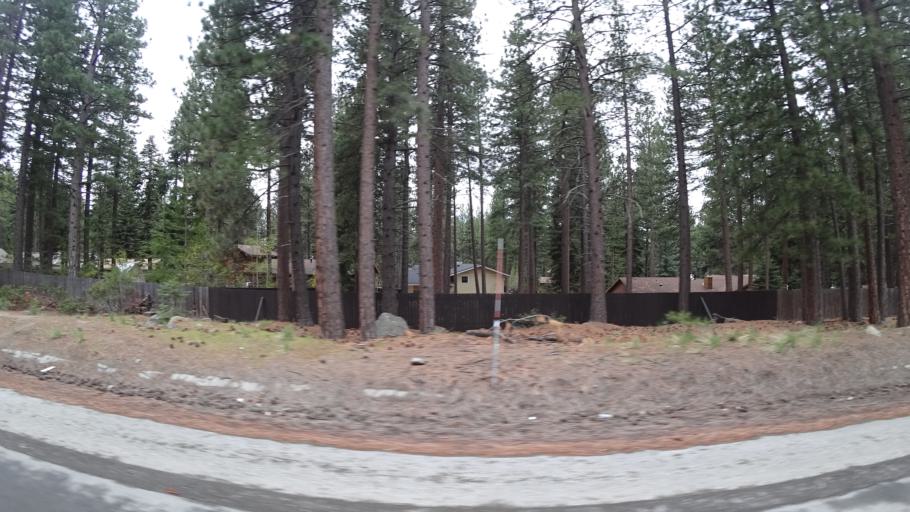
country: US
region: Nevada
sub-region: Washoe County
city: Incline Village
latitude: 39.2431
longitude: -119.9343
